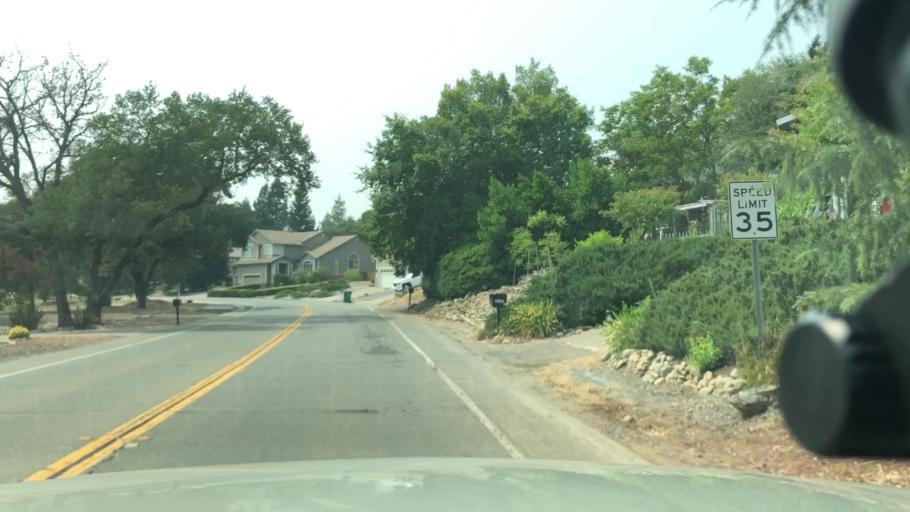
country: US
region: California
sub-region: El Dorado County
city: Cameron Park
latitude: 38.6611
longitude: -121.0026
